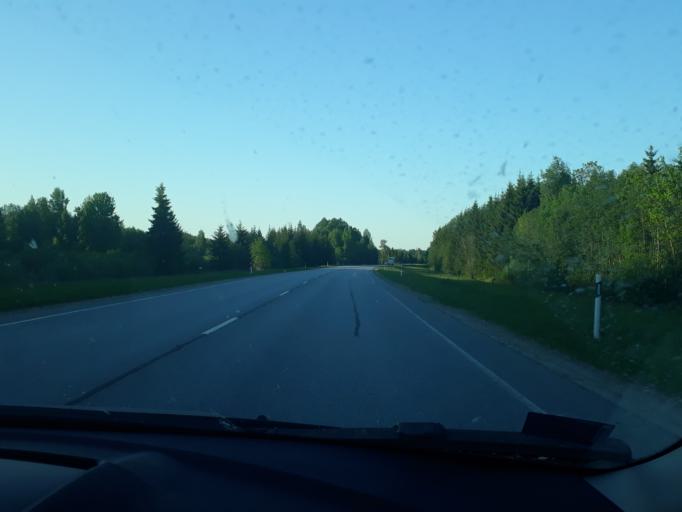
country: EE
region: Paernumaa
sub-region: Sindi linn
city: Sindi
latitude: 58.4608
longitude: 24.6999
